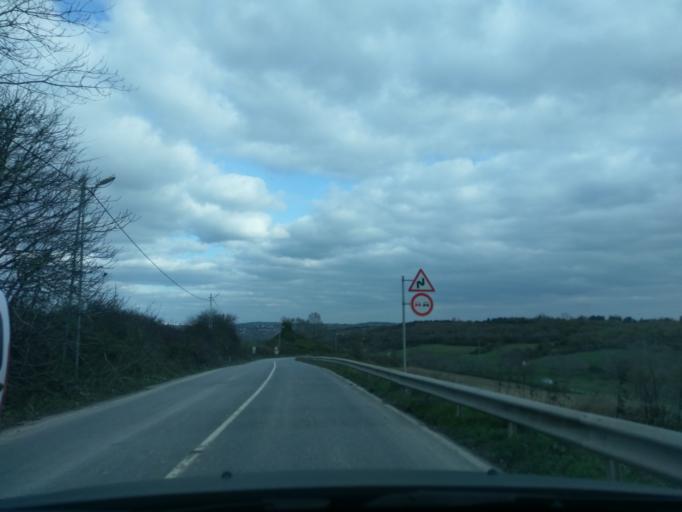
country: TR
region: Istanbul
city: Durusu
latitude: 41.2773
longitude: 28.6617
